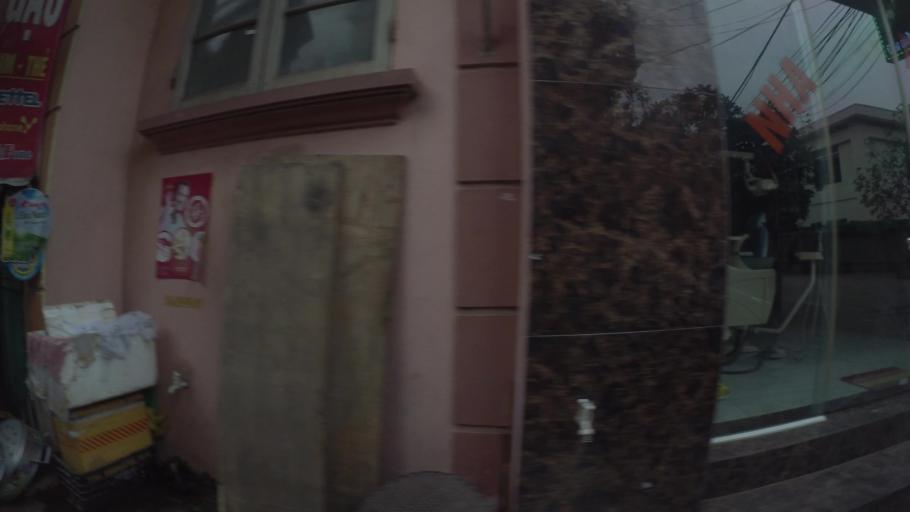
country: VN
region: Ha Noi
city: Hai BaTrung
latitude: 20.9978
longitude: 105.8863
